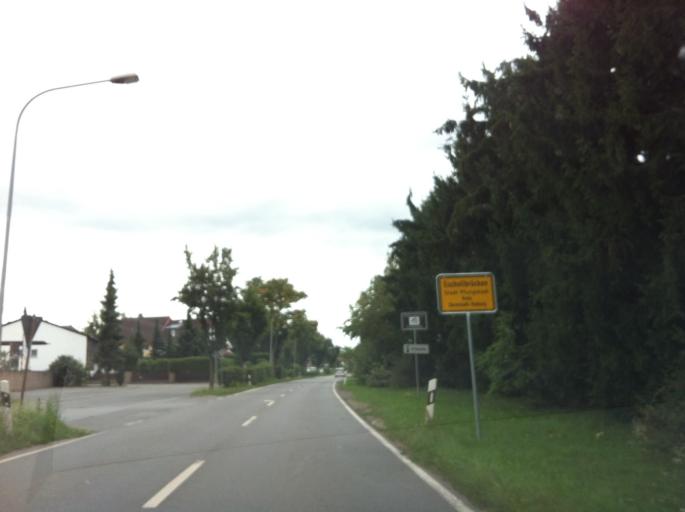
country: DE
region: Hesse
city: Pfungstadt
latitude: 49.8177
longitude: 8.5694
